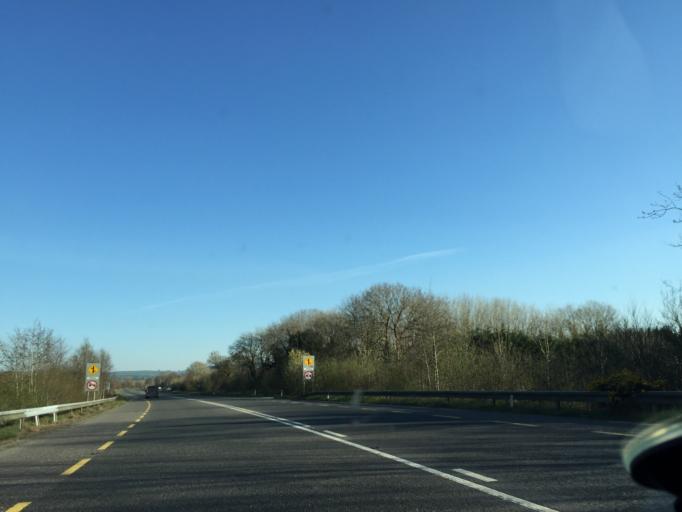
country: IE
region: Munster
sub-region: Ciarrai
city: Castleisland
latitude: 52.1958
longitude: -9.5695
